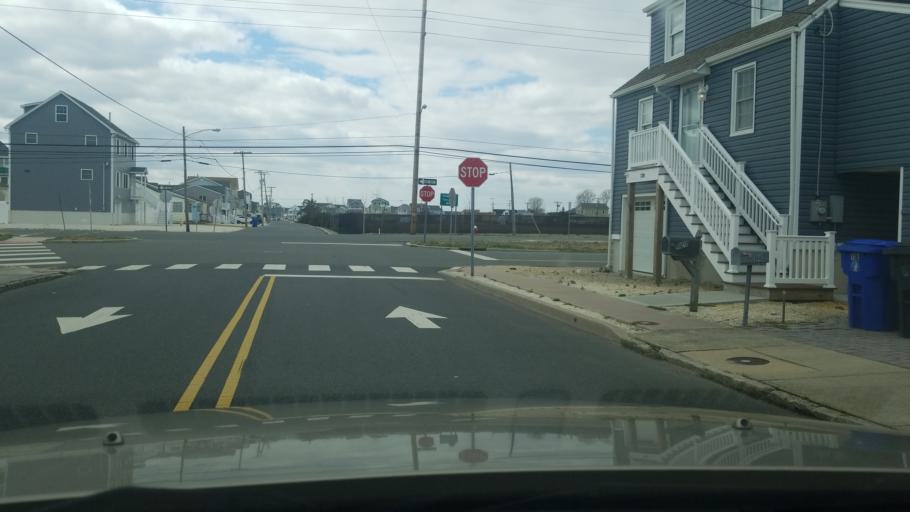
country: US
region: New Jersey
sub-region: Ocean County
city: Dover Beaches South
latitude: 39.9514
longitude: -74.0730
